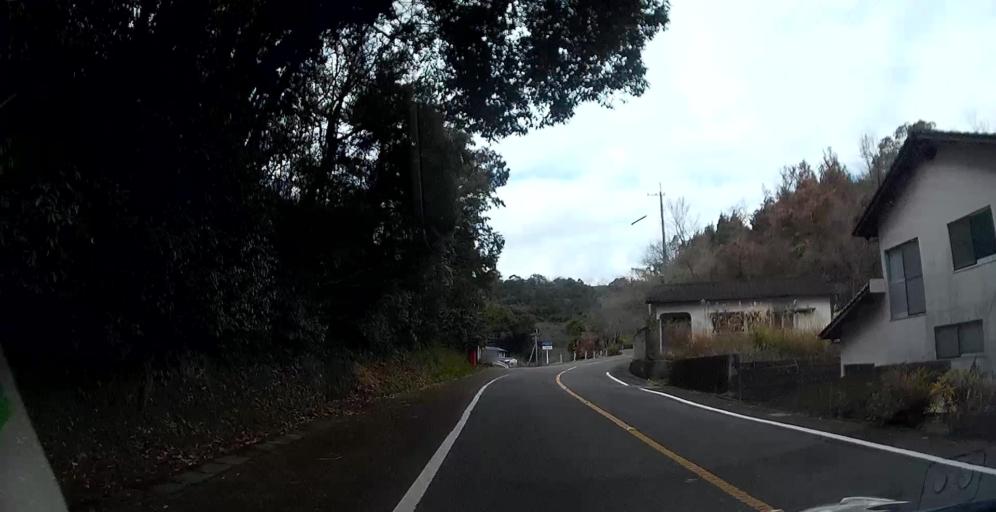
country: JP
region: Kumamoto
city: Minamata
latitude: 32.3630
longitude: 130.4947
